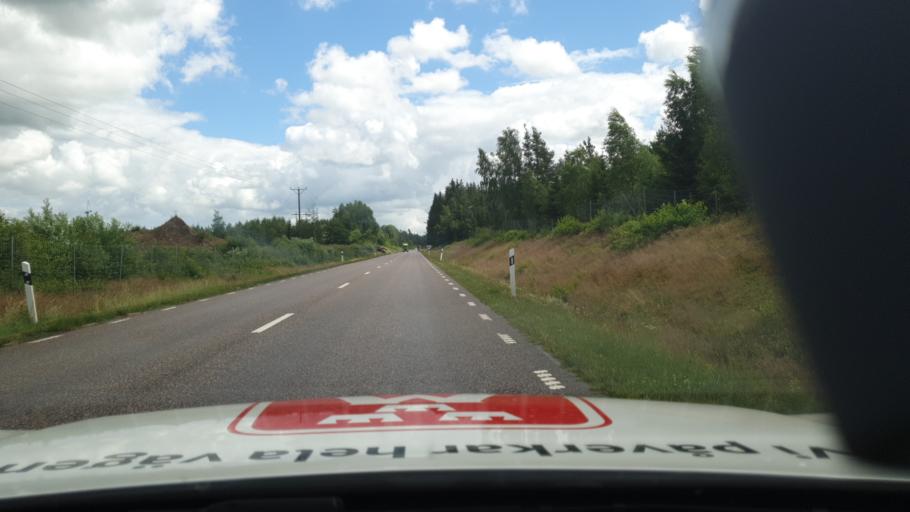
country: SE
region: Vaestra Goetaland
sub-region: Falkopings Kommun
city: Floby
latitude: 58.1800
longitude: 13.3777
